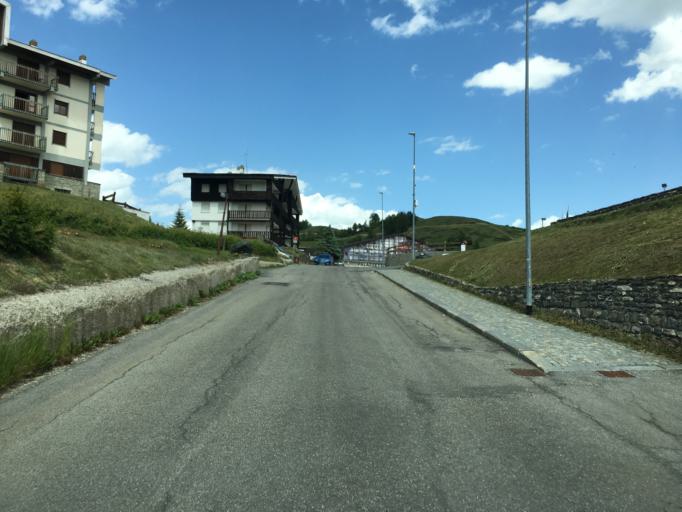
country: IT
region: Piedmont
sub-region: Provincia di Torino
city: Sestriere
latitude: 44.9589
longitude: 6.8760
